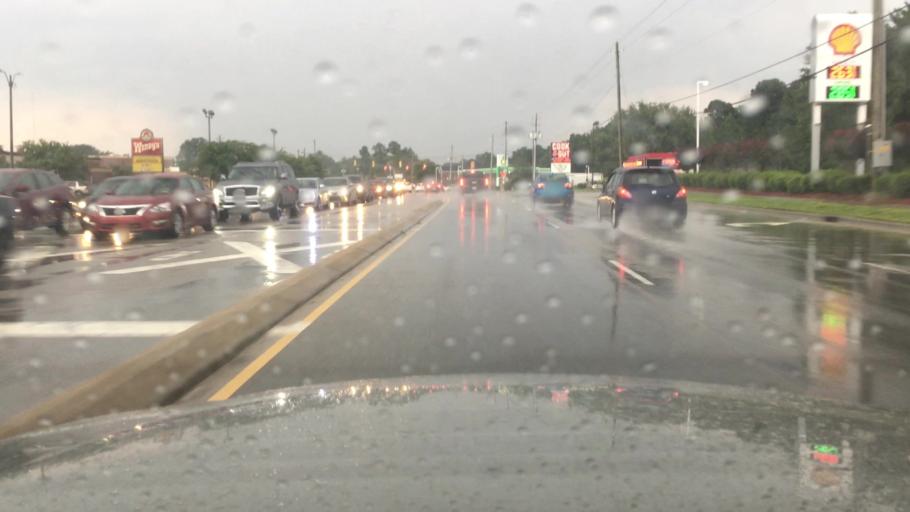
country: US
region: North Carolina
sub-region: Cumberland County
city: Fort Bragg
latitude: 35.0608
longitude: -79.0141
